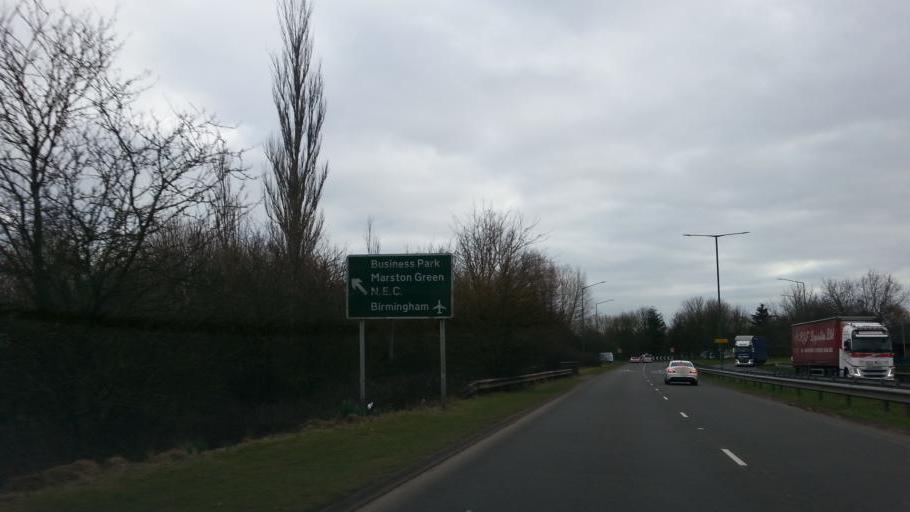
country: GB
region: England
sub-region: Solihull
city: Chelmsley Wood
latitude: 52.4875
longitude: -1.7342
